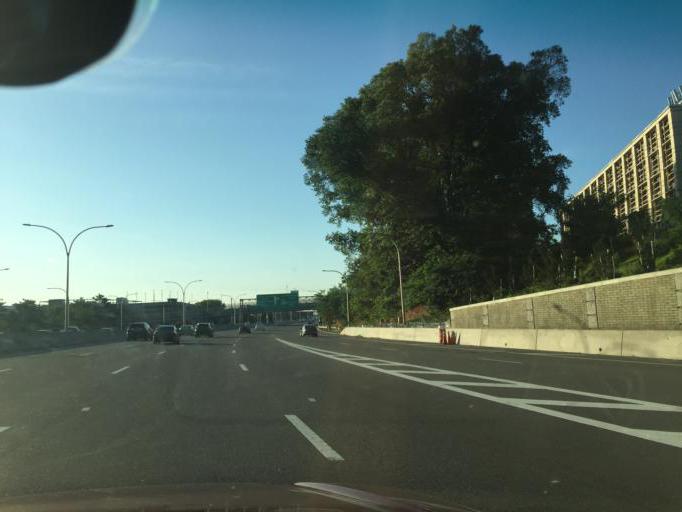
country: US
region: New York
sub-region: Bronx
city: The Bronx
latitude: 40.7712
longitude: -73.8705
